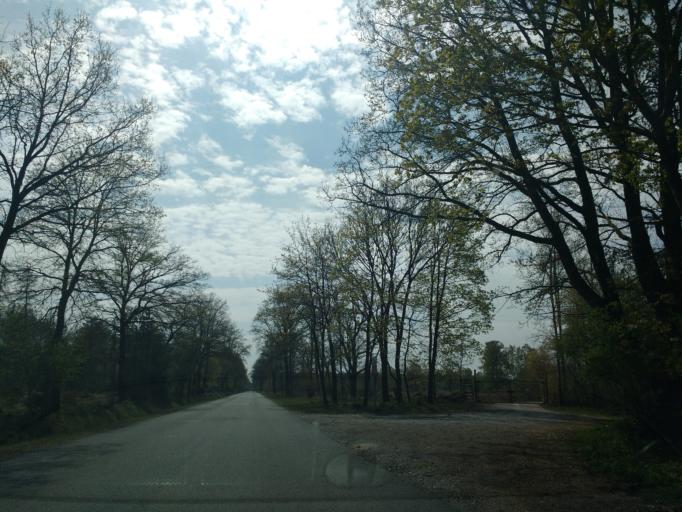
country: DE
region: North Rhine-Westphalia
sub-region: Regierungsbezirk Detmold
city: Hovelhof
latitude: 51.8151
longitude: 8.7225
